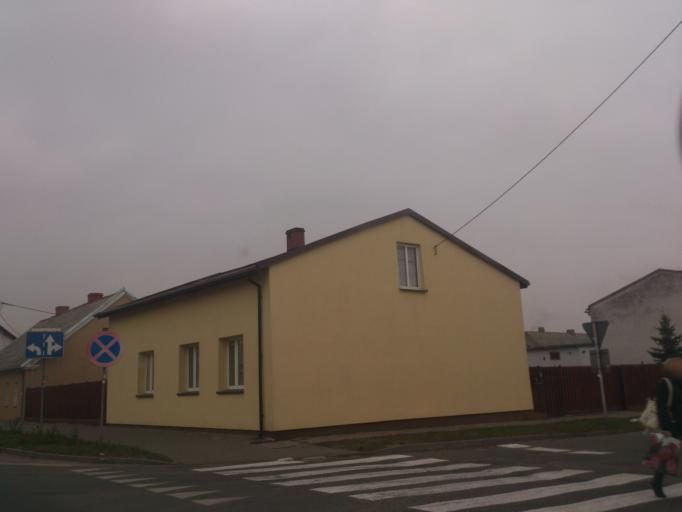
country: PL
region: Kujawsko-Pomorskie
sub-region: Powiat golubsko-dobrzynski
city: Golub-Dobrzyn
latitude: 53.1077
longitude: 19.0584
